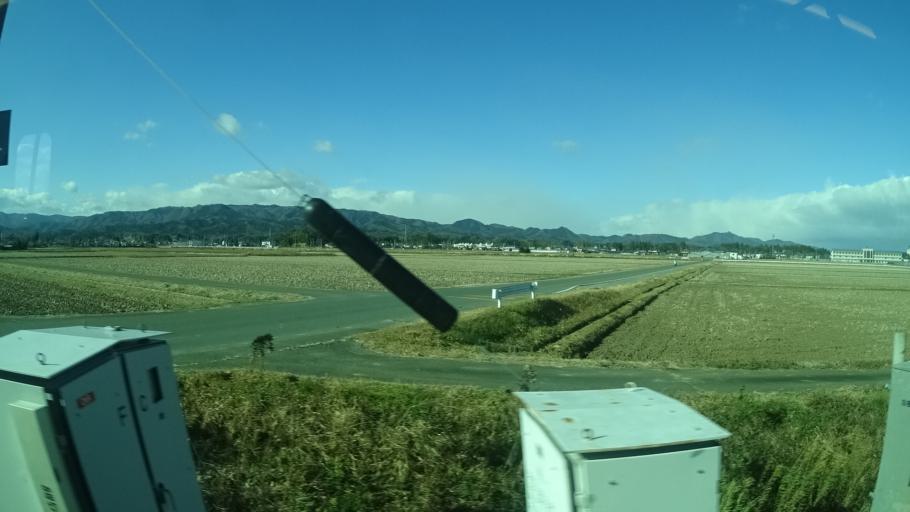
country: JP
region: Miyagi
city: Marumori
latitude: 37.7858
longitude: 140.9224
